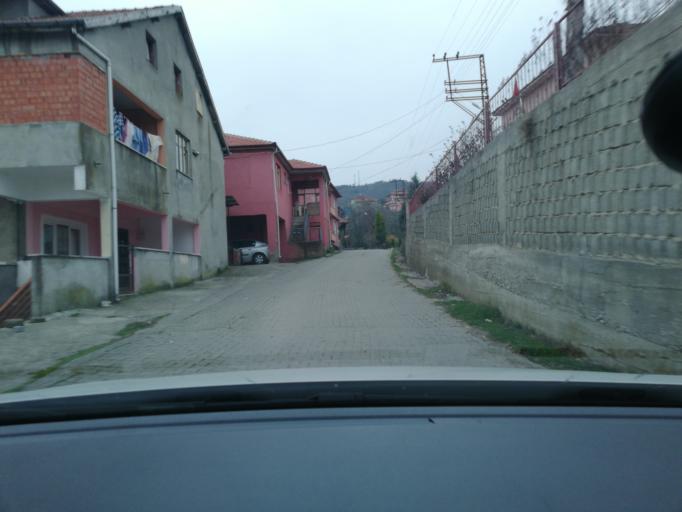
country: TR
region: Zonguldak
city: Saltukova
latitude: 41.5186
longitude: 32.0667
